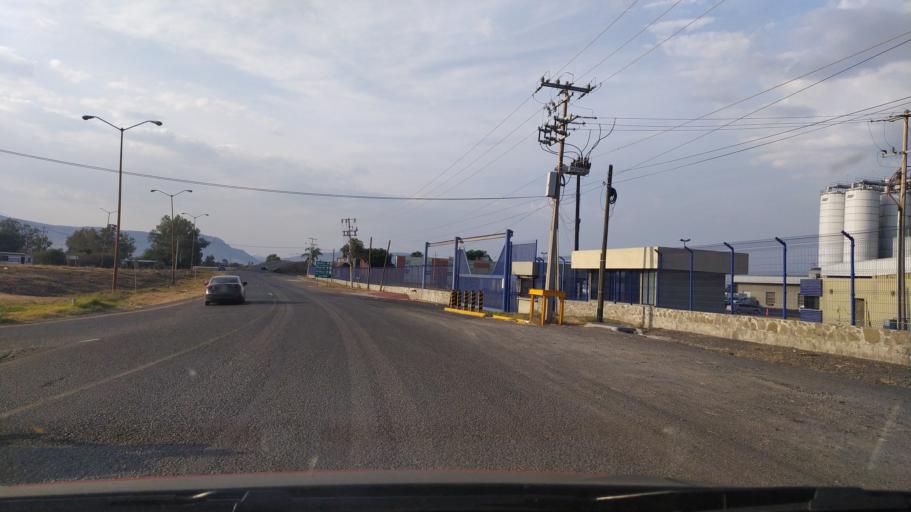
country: MX
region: Jalisco
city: La Barca
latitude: 20.3184
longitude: -102.5364
